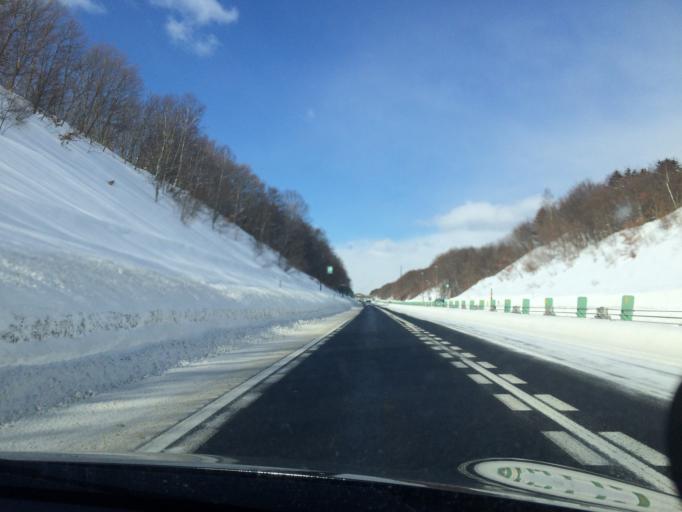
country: JP
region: Hokkaido
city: Kitahiroshima
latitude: 42.9251
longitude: 141.5393
